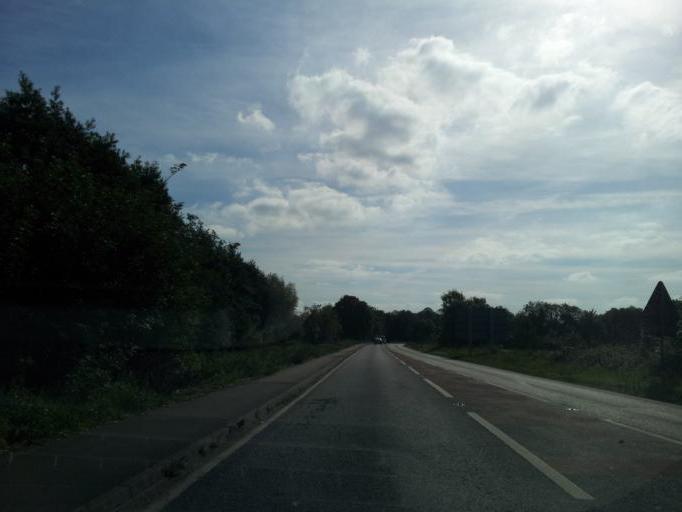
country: GB
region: England
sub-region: Cambridgeshire
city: Waterbeach
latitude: 52.2705
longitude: 0.1788
